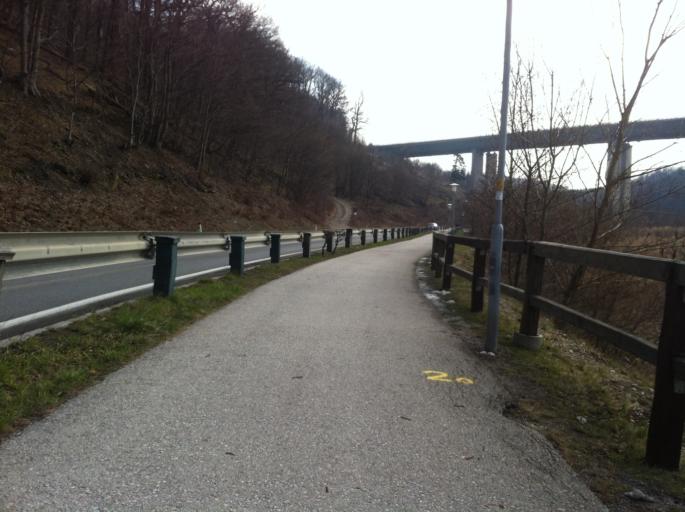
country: AT
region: Lower Austria
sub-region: Politischer Bezirk Wien-Umgebung
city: Wolfsgraben
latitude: 48.1783
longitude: 16.1233
